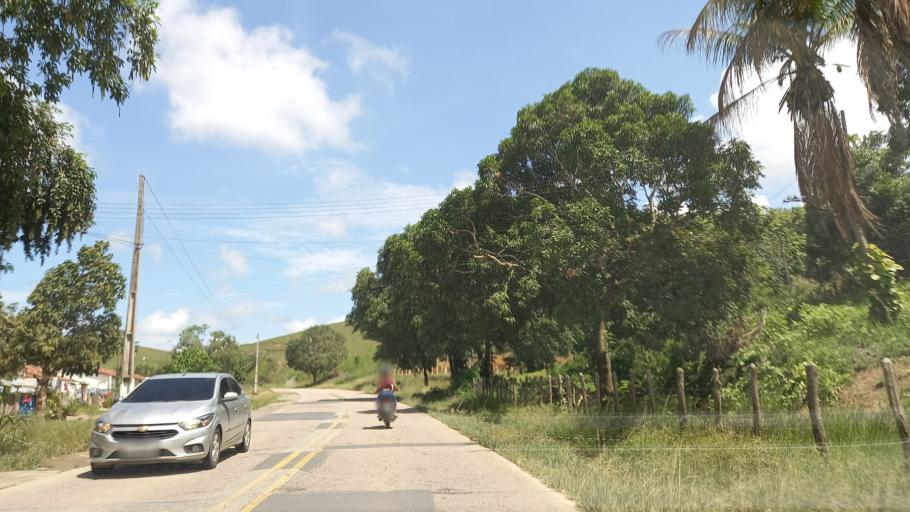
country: BR
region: Pernambuco
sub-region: Barreiros
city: Barreiros
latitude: -8.7506
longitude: -35.1718
